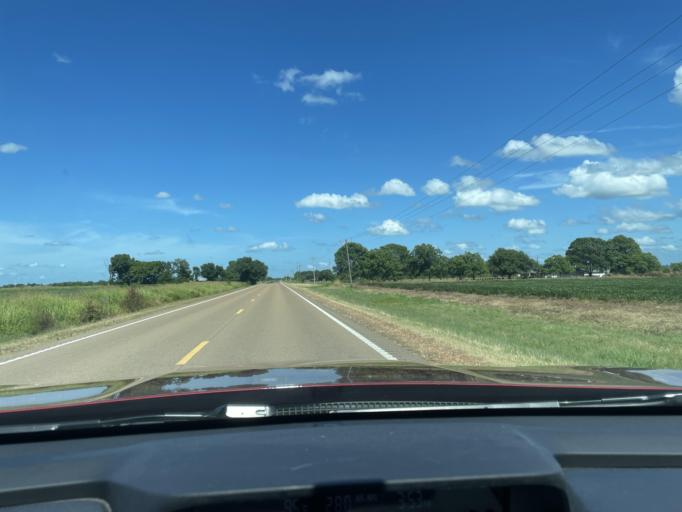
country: US
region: Mississippi
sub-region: Washington County
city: Hollandale
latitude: 33.1843
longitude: -90.6744
